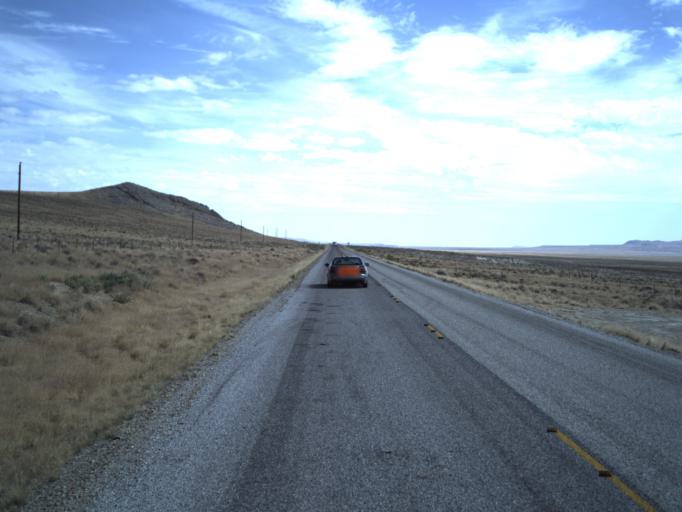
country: US
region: Utah
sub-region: Tooele County
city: Wendover
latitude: 41.4522
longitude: -113.6669
